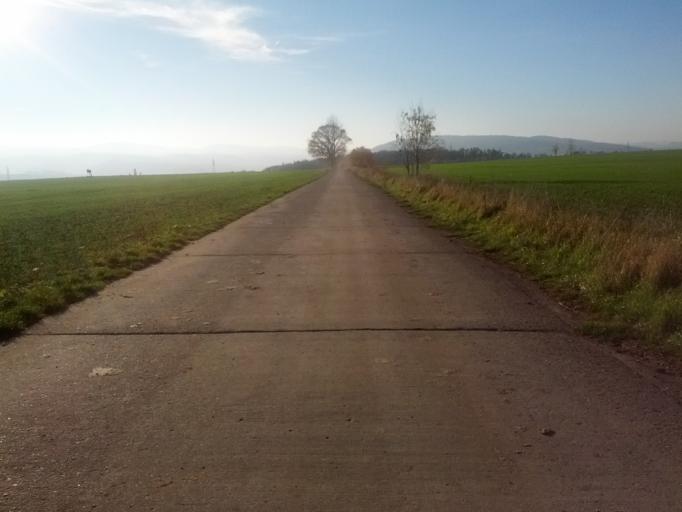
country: DE
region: Thuringia
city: Mechterstadt
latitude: 50.9600
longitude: 10.5374
